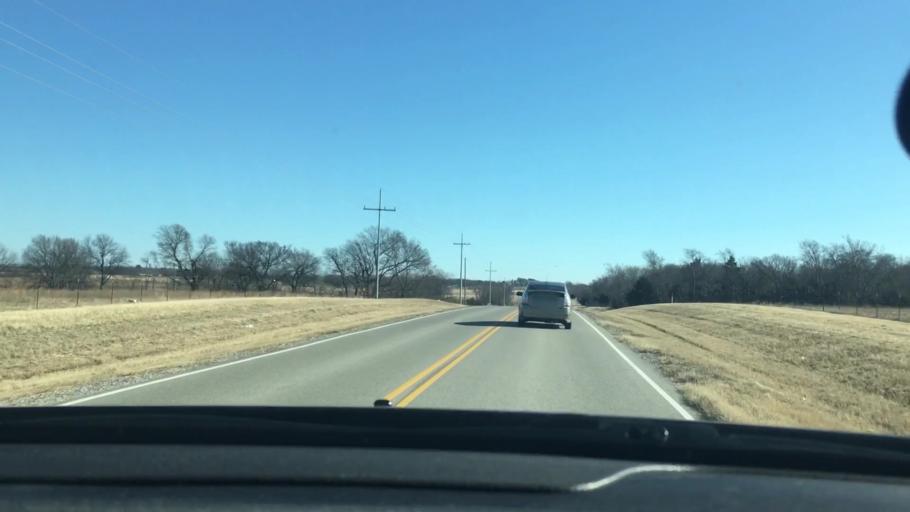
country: US
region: Oklahoma
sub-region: Murray County
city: Davis
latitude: 34.4772
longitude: -97.0750
